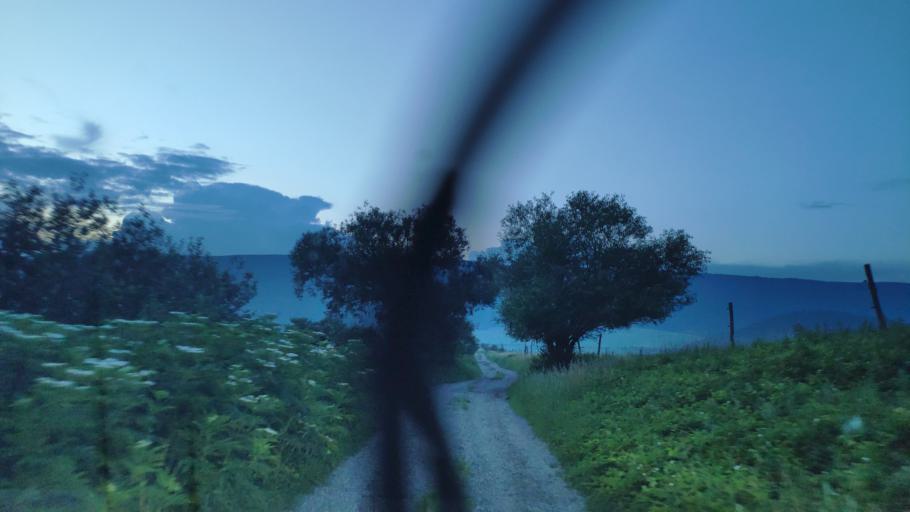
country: SK
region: Kosicky
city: Medzev
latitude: 48.5851
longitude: 20.8026
